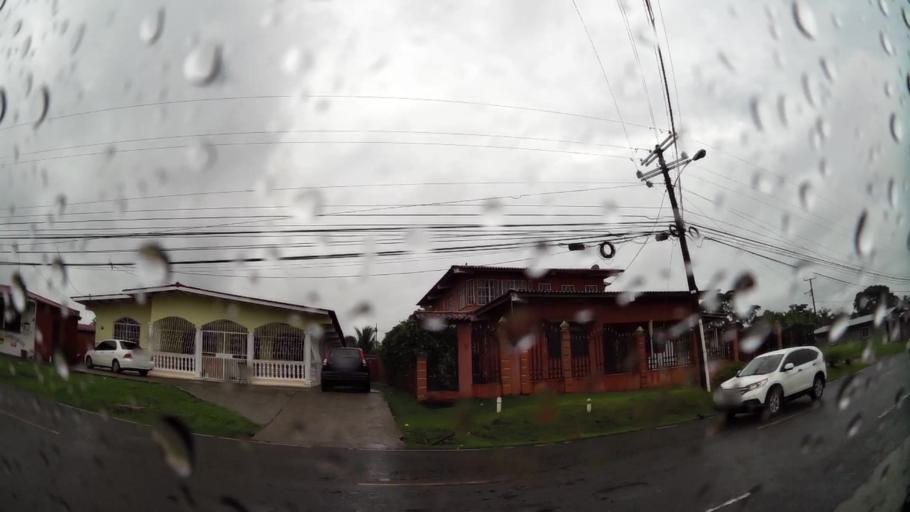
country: PA
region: Colon
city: Arco Iris
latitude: 9.3378
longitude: -79.8724
